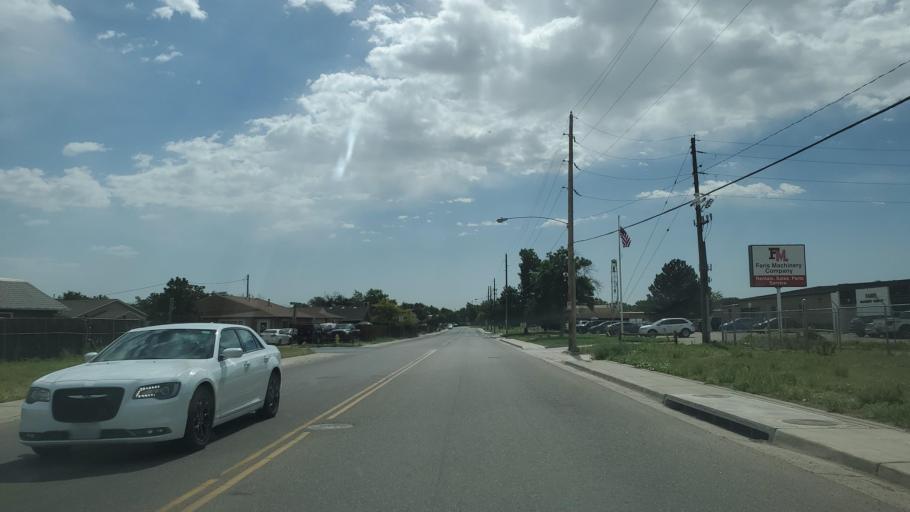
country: US
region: Colorado
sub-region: Adams County
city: Derby
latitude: 39.8364
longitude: -104.9220
